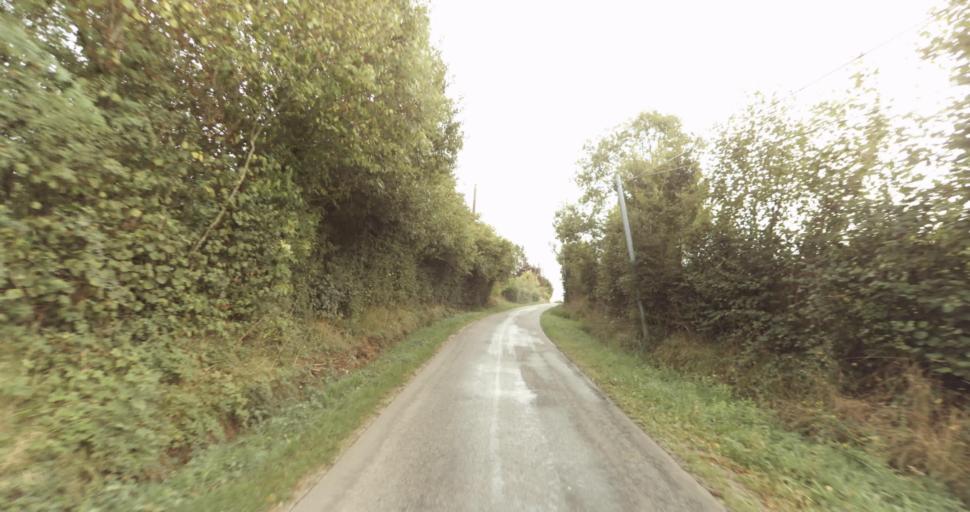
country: FR
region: Lower Normandy
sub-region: Departement de l'Orne
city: Sainte-Gauburge-Sainte-Colombe
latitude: 48.7027
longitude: 0.3371
